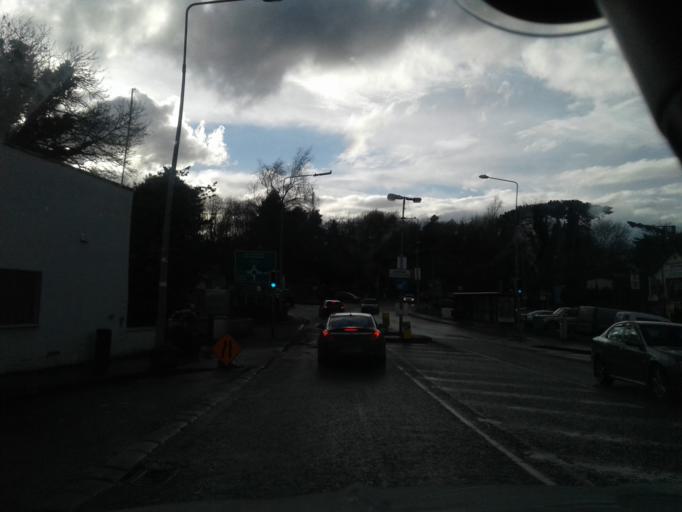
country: IE
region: Ulster
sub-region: County Donegal
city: Leifear
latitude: 54.8317
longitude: -7.4820
